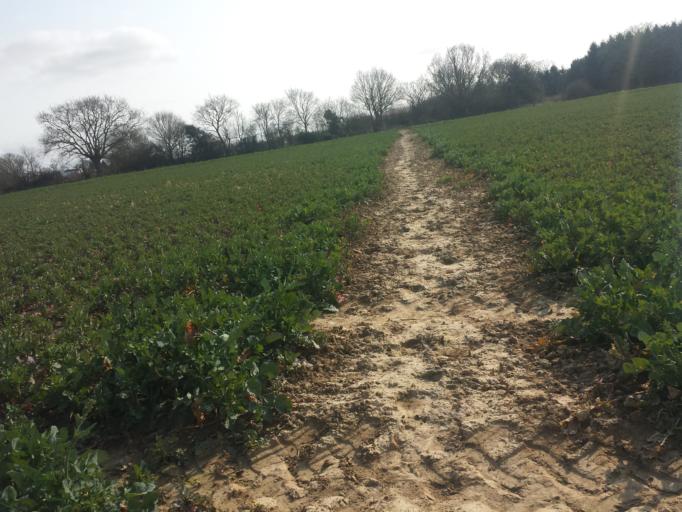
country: GB
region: England
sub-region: Essex
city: Little Clacton
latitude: 51.8897
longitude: 1.1625
